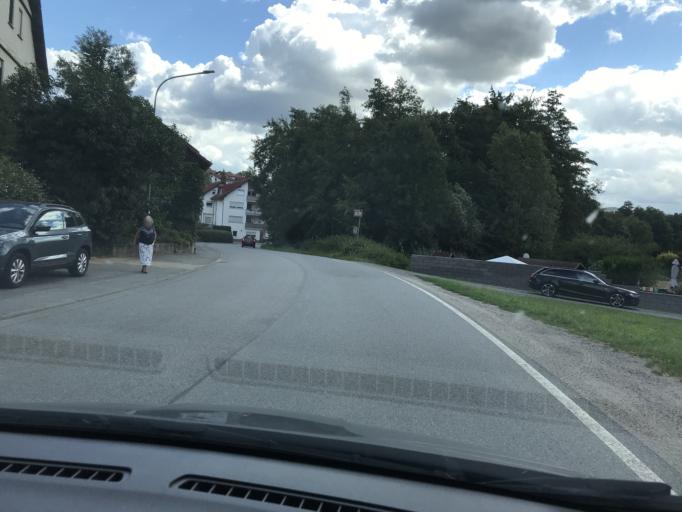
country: DE
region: Hesse
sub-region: Regierungsbezirk Darmstadt
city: Furth
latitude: 49.6567
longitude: 8.7528
